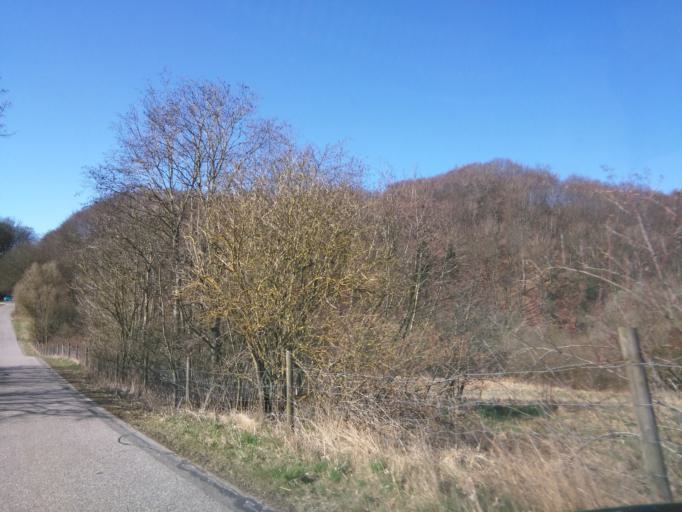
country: DK
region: Central Jutland
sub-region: Skanderborg Kommune
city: Stilling
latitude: 56.0942
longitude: 9.9828
